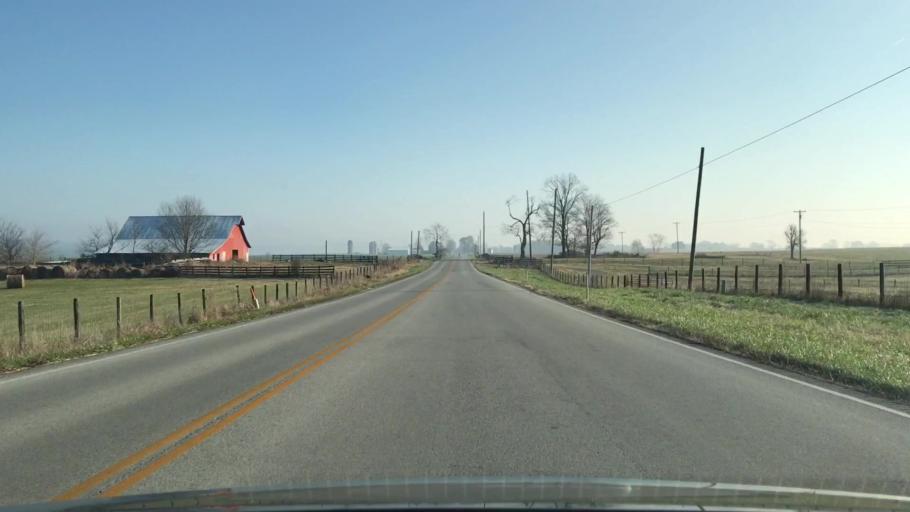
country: US
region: Kentucky
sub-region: Edmonson County
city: Brownsville
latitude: 37.0752
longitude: -86.2550
